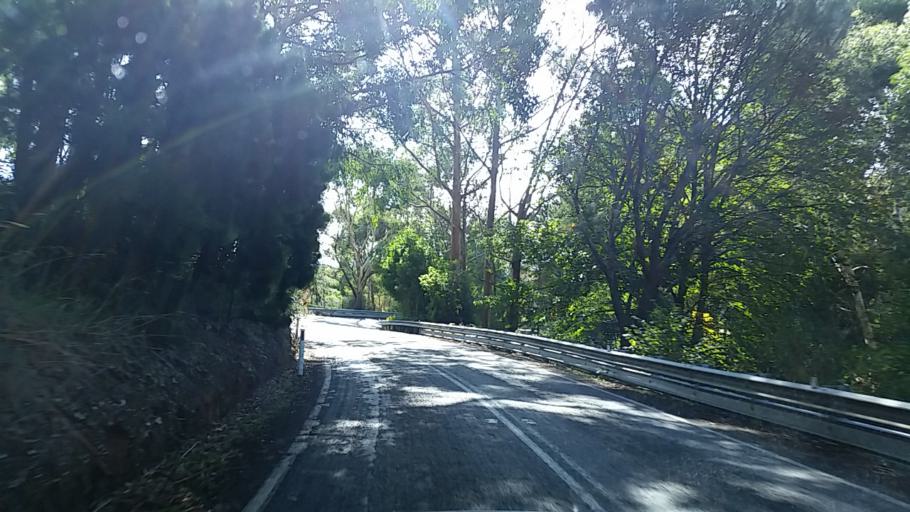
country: AU
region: South Australia
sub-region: Adelaide Hills
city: Adelaide Hills
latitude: -34.9563
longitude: 138.7175
